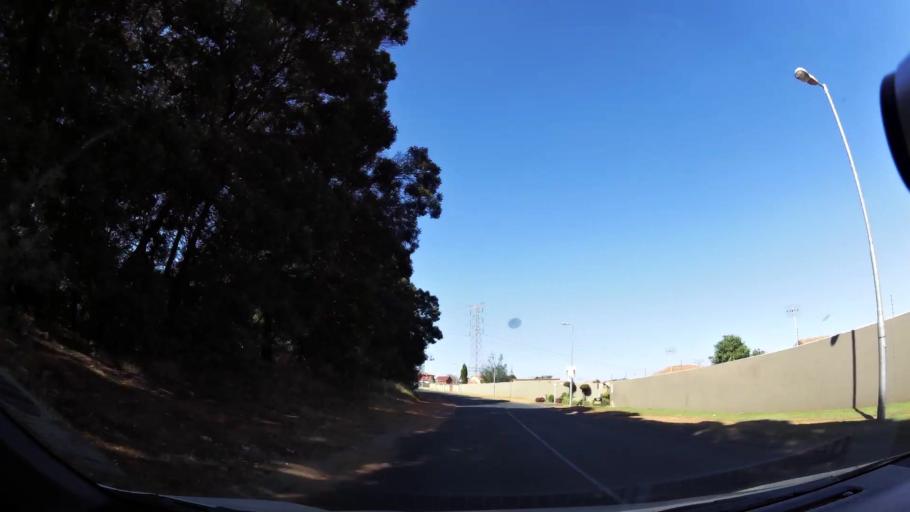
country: ZA
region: Gauteng
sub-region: City of Johannesburg Metropolitan Municipality
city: Johannesburg
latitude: -26.2637
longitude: 27.9890
